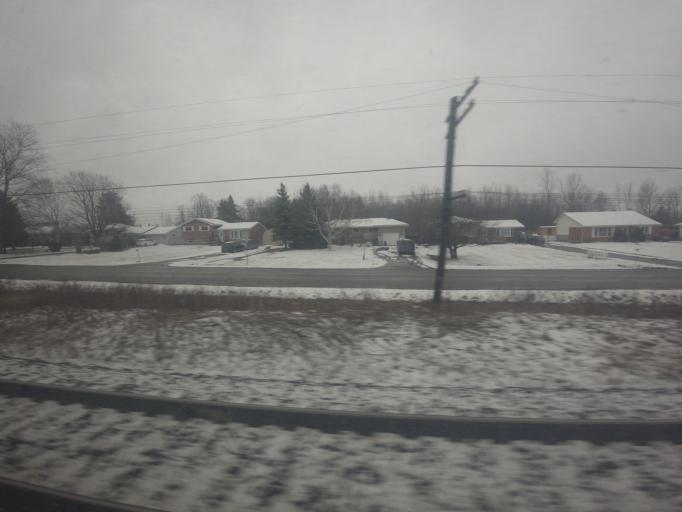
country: CA
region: Ontario
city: Belleville
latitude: 44.1562
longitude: -77.4579
